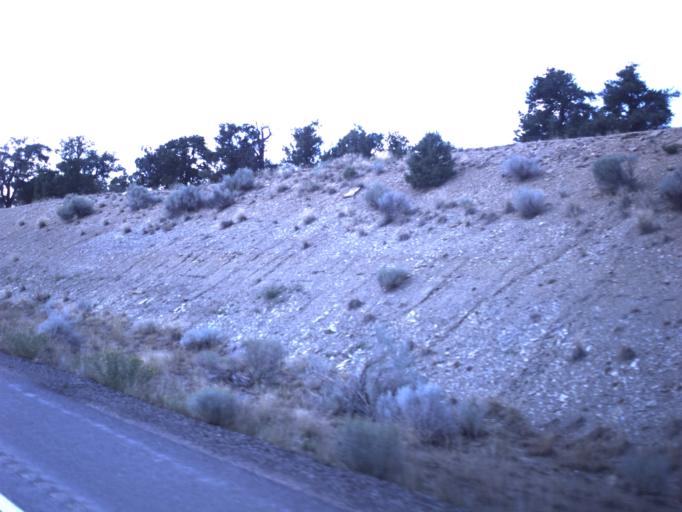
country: US
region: Utah
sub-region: Duchesne County
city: Duchesne
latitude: 40.1786
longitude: -110.6001
